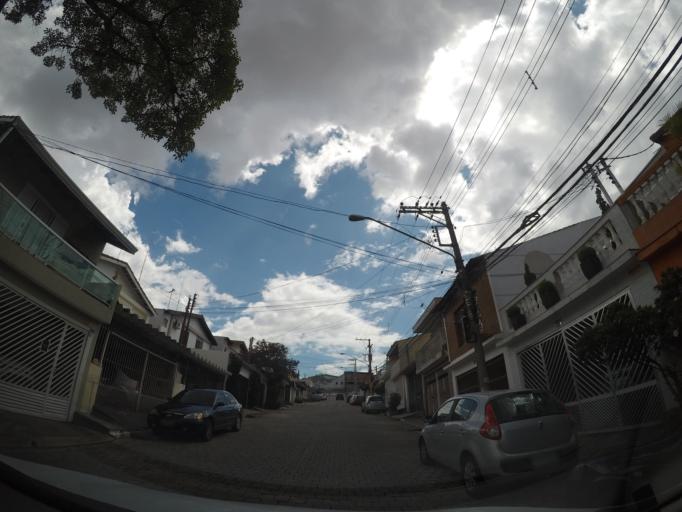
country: BR
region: Sao Paulo
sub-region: Guarulhos
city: Guarulhos
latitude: -23.4562
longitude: -46.5363
